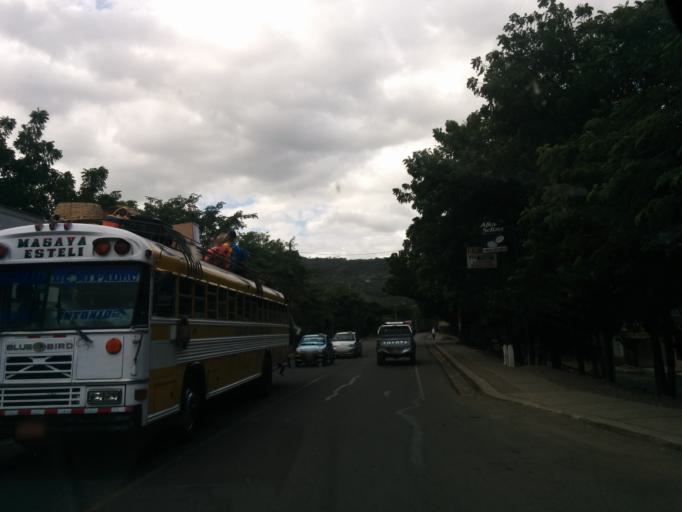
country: NI
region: Esteli
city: Esteli
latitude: 12.9617
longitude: -86.2305
